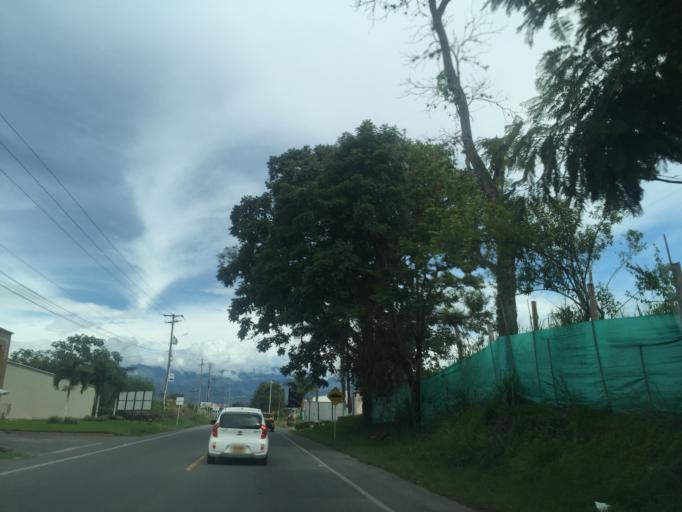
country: CO
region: Quindio
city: Armenia
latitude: 4.5278
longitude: -75.7175
